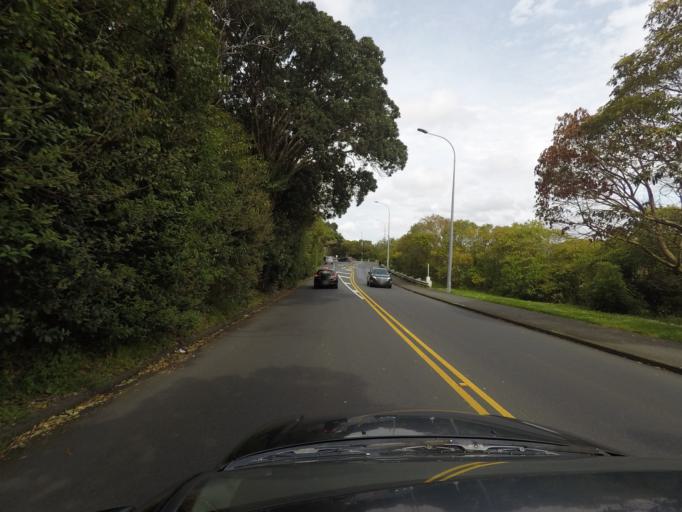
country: NZ
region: Auckland
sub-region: Auckland
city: Auckland
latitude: -36.8603
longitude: 174.8120
